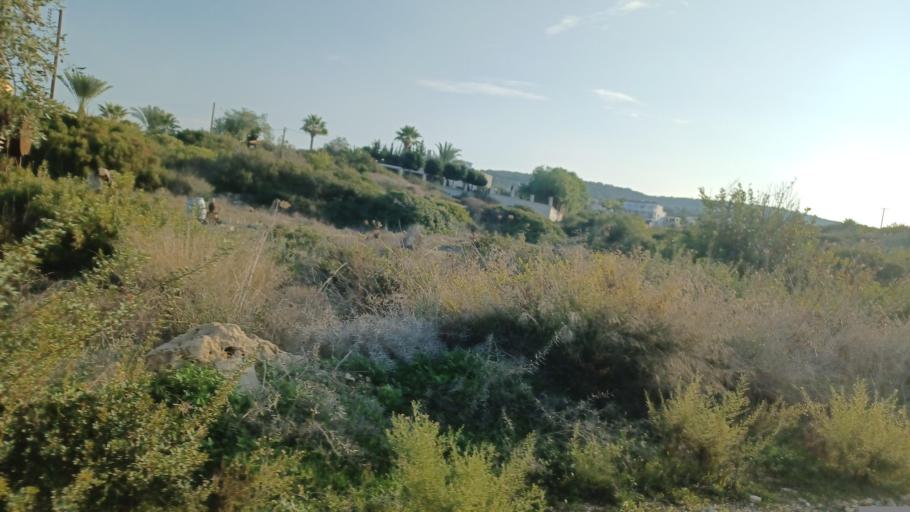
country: CY
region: Pafos
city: Pegeia
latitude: 34.8952
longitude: 32.3390
